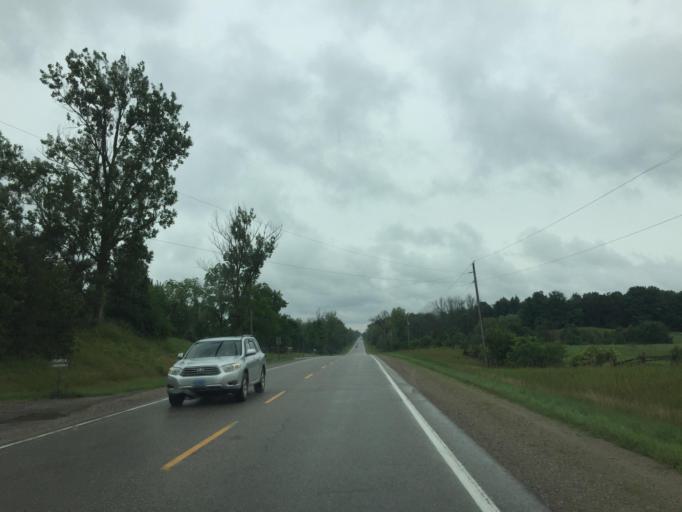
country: CA
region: Ontario
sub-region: Wellington County
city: Guelph
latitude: 43.4564
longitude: -80.2179
